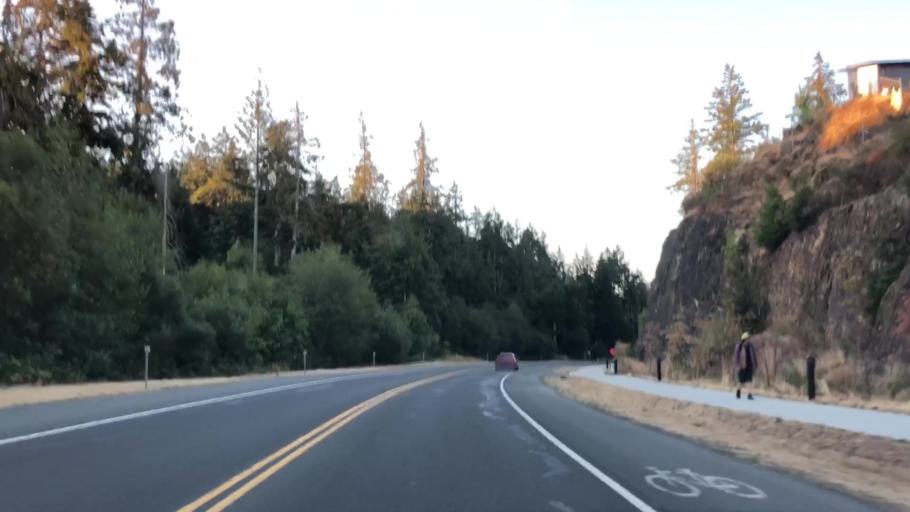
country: CA
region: British Columbia
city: Colwood
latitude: 48.4163
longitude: -123.5049
